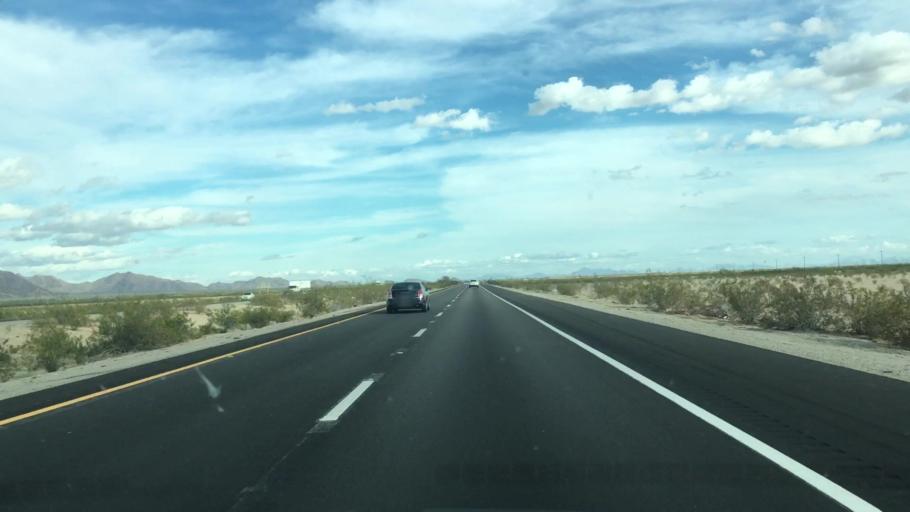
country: US
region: California
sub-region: Riverside County
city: Mesa Verde
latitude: 33.6080
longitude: -114.8894
